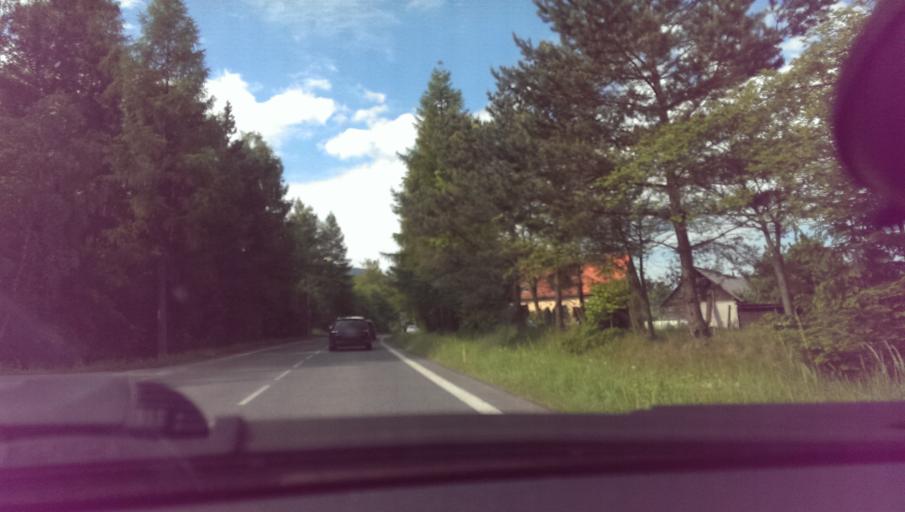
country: CZ
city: Trojanovice
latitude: 49.5255
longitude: 18.2441
